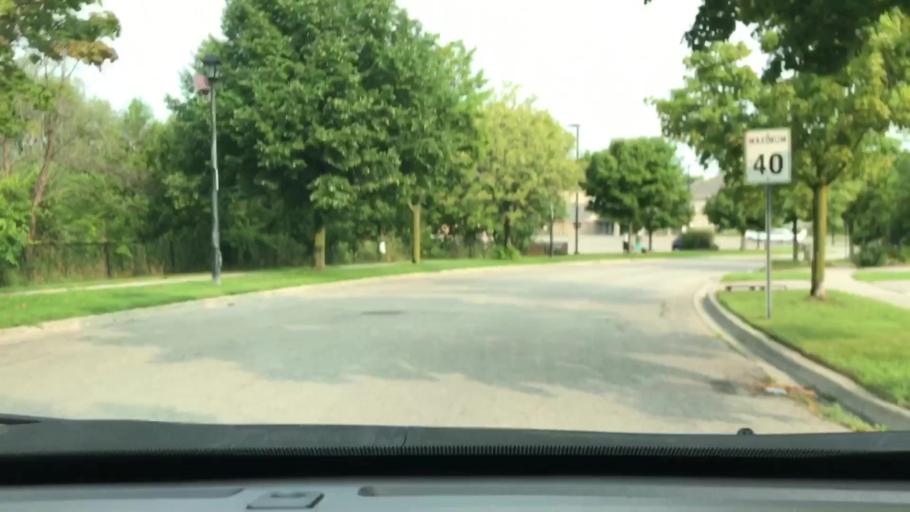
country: CA
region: Ontario
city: Newmarket
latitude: 44.0537
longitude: -79.4319
